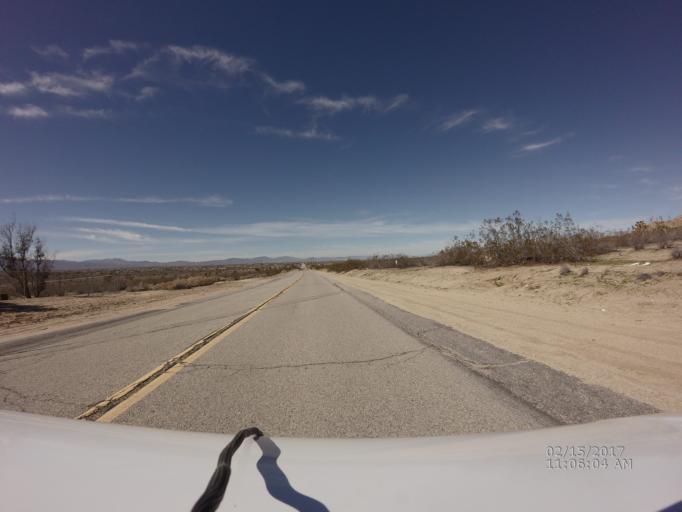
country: US
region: California
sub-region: Los Angeles County
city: Lake Los Angeles
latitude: 34.5873
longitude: -117.8600
